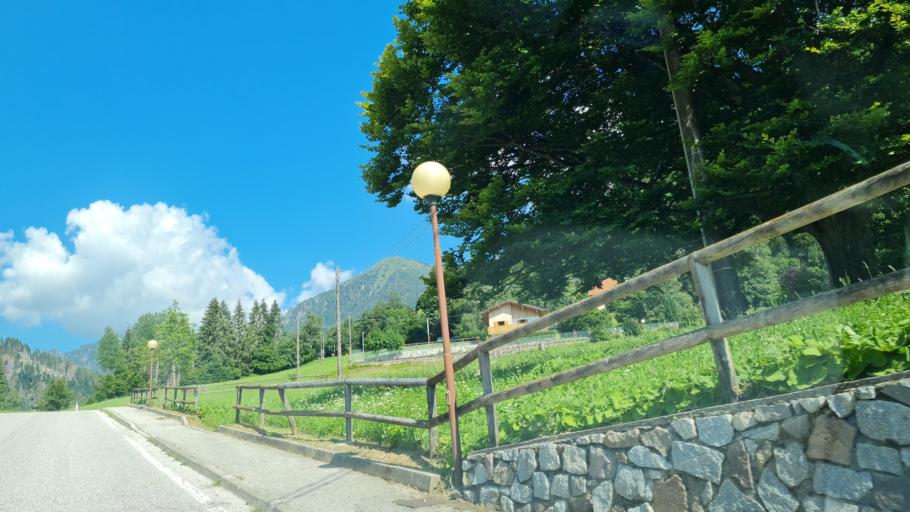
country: IT
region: Trentino-Alto Adige
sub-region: Provincia di Trento
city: Telve di Sopra
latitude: 46.1380
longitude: 11.4718
